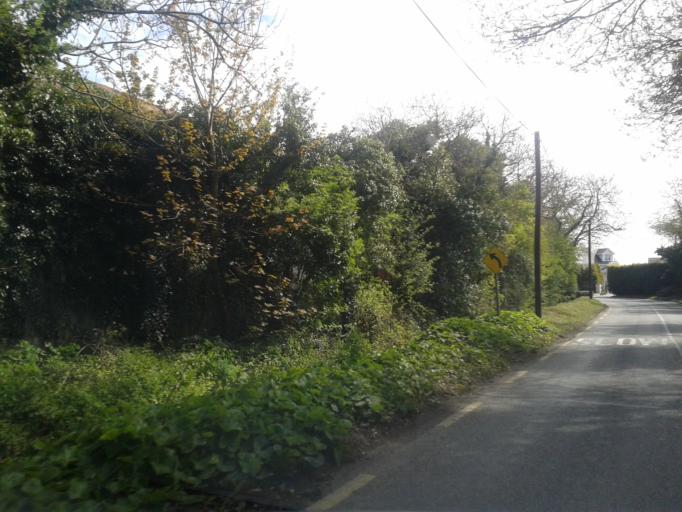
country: IE
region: Leinster
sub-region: Fingal County
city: Swords
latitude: 53.4390
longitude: -6.2508
